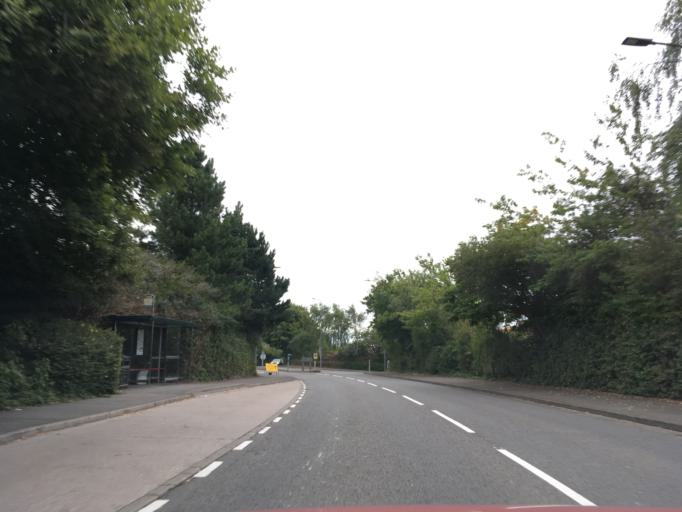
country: GB
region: Wales
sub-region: Caerphilly County Borough
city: Machen
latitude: 51.5349
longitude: -3.1441
